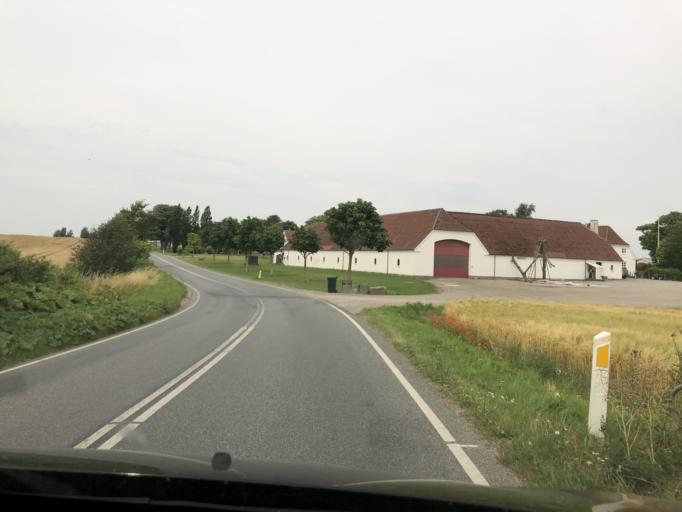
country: DK
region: South Denmark
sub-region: Assens Kommune
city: Glamsbjerg
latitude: 55.2929
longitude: 10.0761
